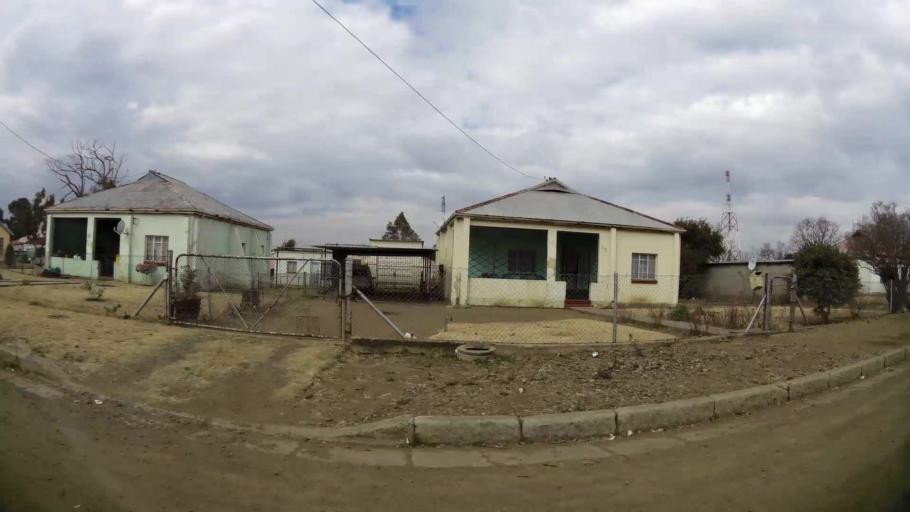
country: ZA
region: Orange Free State
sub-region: Fezile Dabi District Municipality
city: Kroonstad
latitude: -27.6564
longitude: 27.2351
